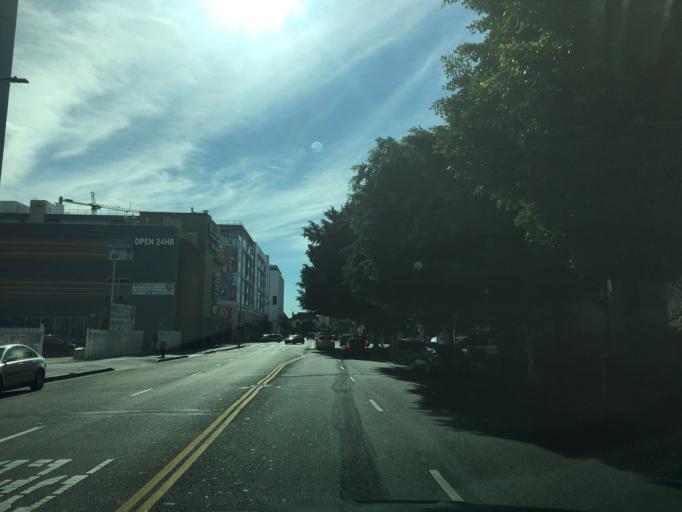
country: US
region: California
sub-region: Los Angeles County
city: Silver Lake
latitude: 34.0646
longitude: -118.2871
